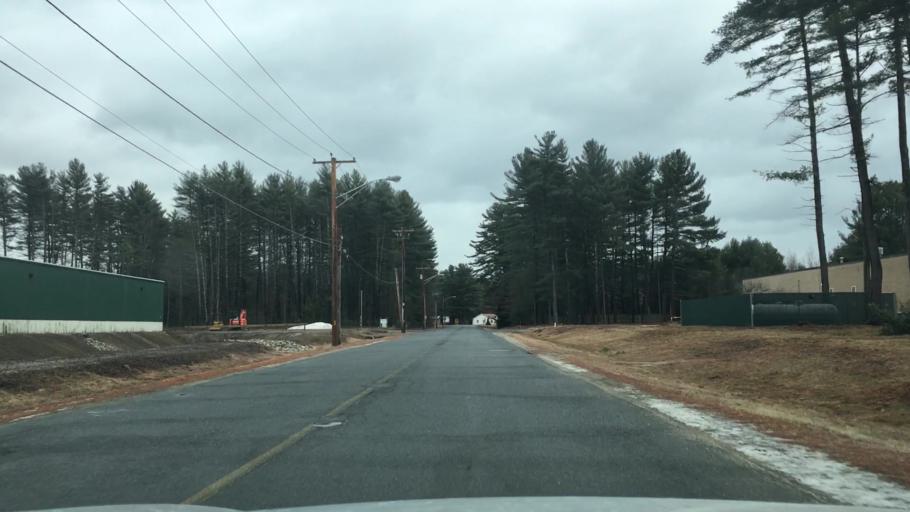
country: US
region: Massachusetts
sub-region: Franklin County
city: Orange
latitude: 42.5640
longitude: -72.2846
